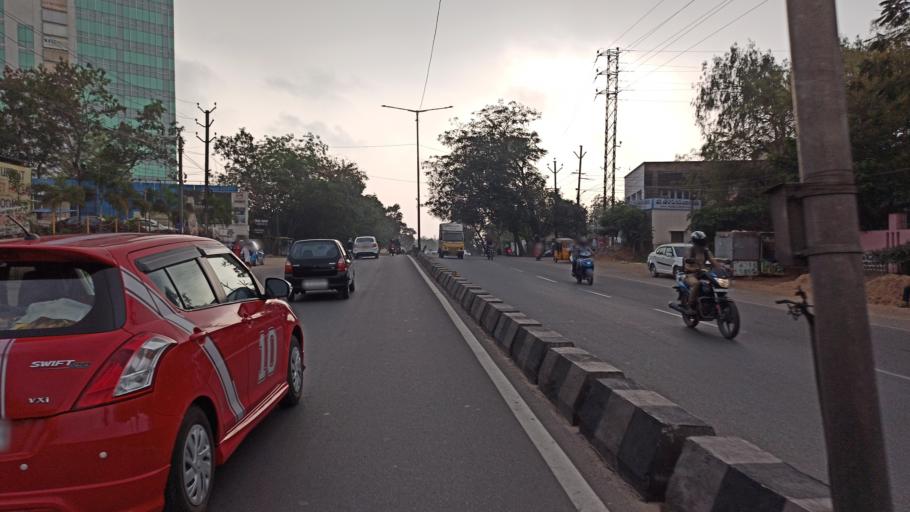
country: IN
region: Telangana
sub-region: Rangareddi
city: Uppal Kalan
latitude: 17.4012
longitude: 78.5449
